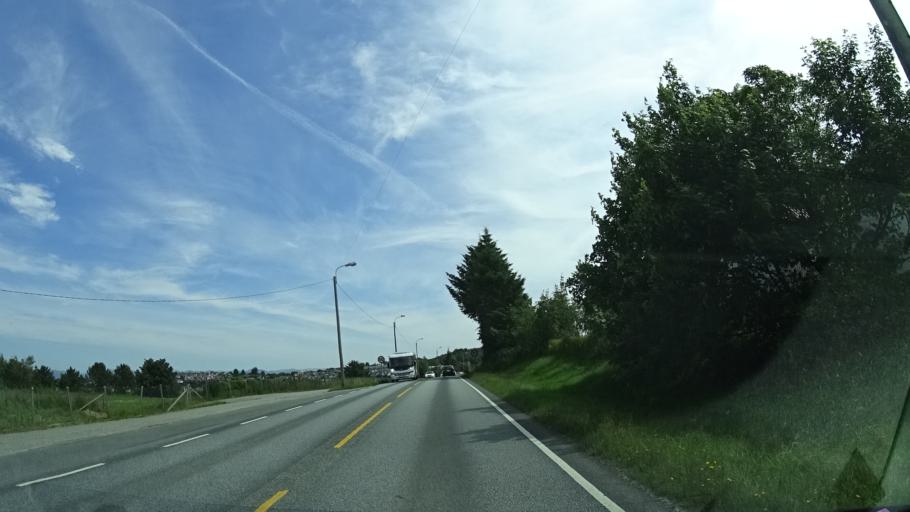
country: NO
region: Rogaland
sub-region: Randaberg
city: Randaberg
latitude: 58.9894
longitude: 5.6600
